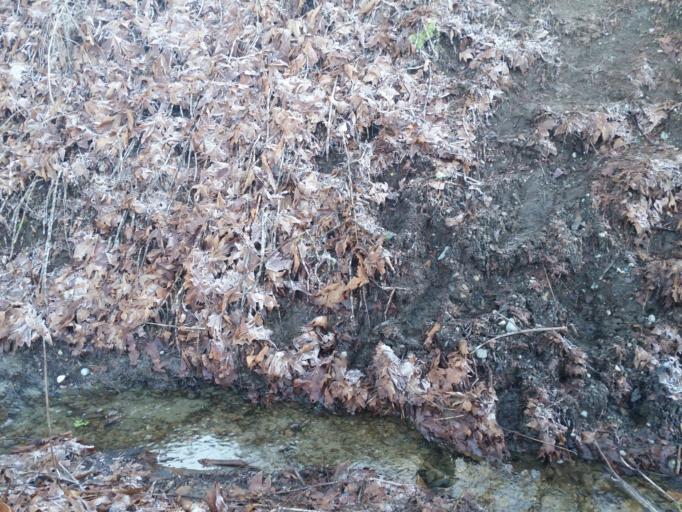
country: US
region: Washington
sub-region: King County
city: Woodinville
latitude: 47.7454
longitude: -122.1644
